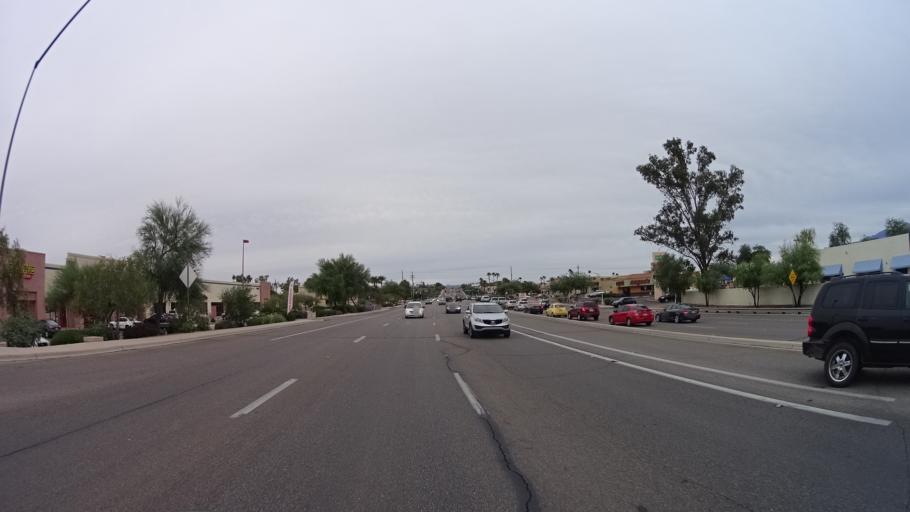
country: US
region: Arizona
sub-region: Pima County
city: Casas Adobes
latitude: 32.3354
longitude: -111.0469
